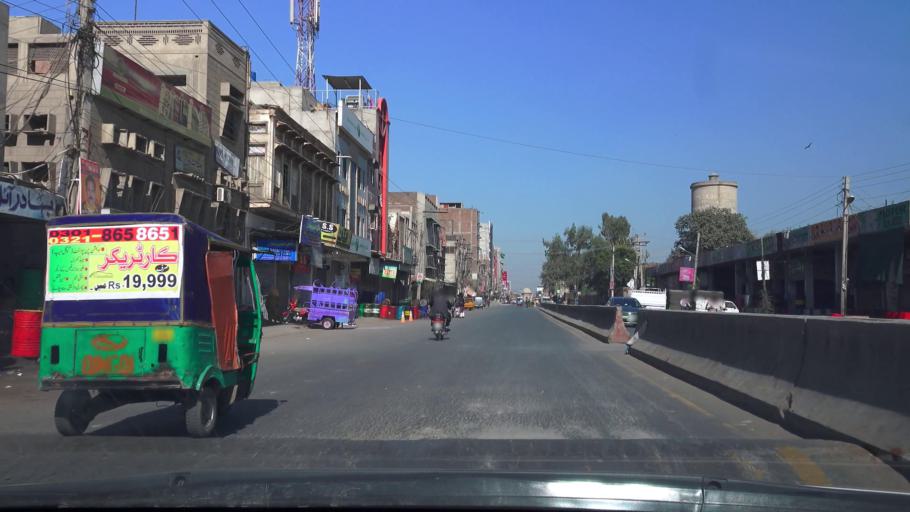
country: PK
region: Punjab
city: Faisalabad
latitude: 31.4154
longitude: 73.0801
